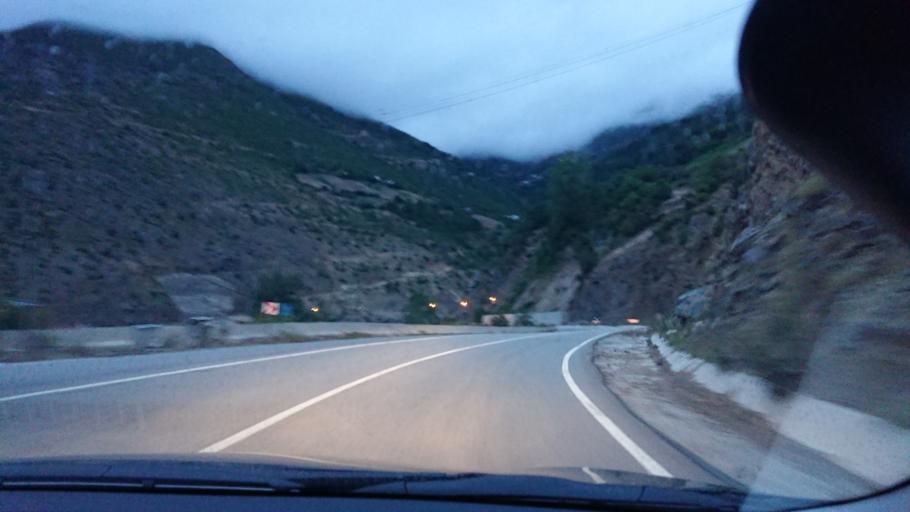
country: TR
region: Gumushane
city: Torul
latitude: 40.6308
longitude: 39.2383
